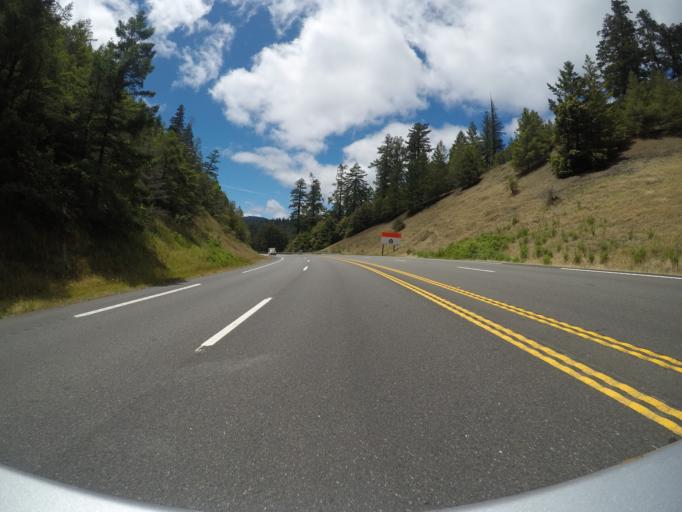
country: US
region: California
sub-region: Humboldt County
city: Redway
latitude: 40.2720
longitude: -123.8548
